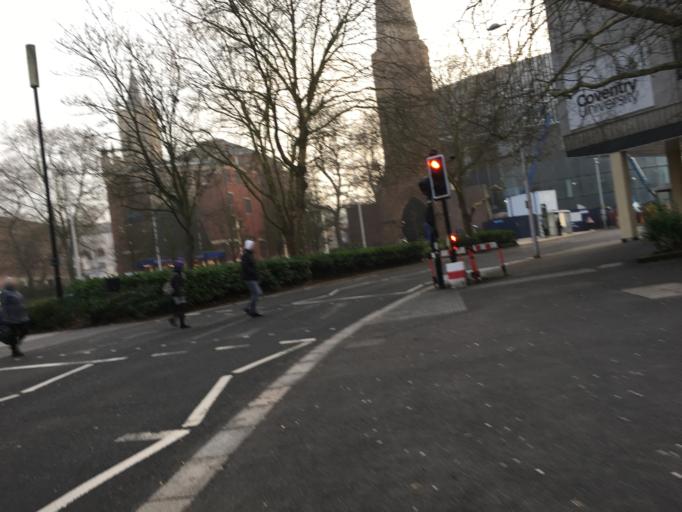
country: GB
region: England
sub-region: Coventry
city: Coventry
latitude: 52.4055
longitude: -1.5126
